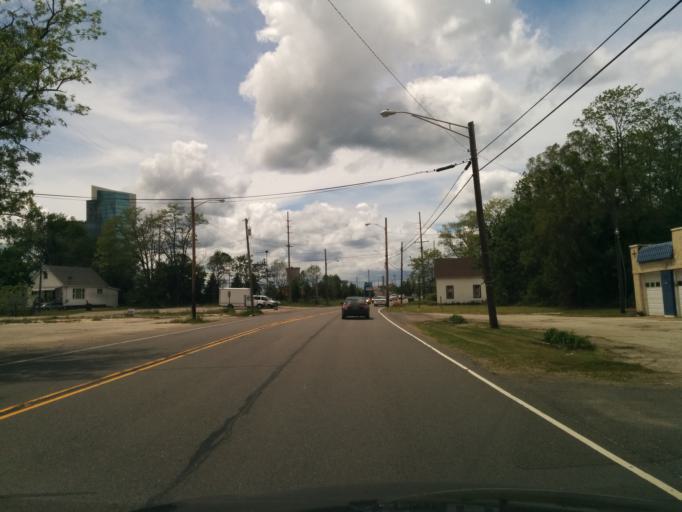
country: US
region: Indiana
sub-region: LaPorte County
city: Michigan City
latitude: 41.7223
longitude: -86.8881
